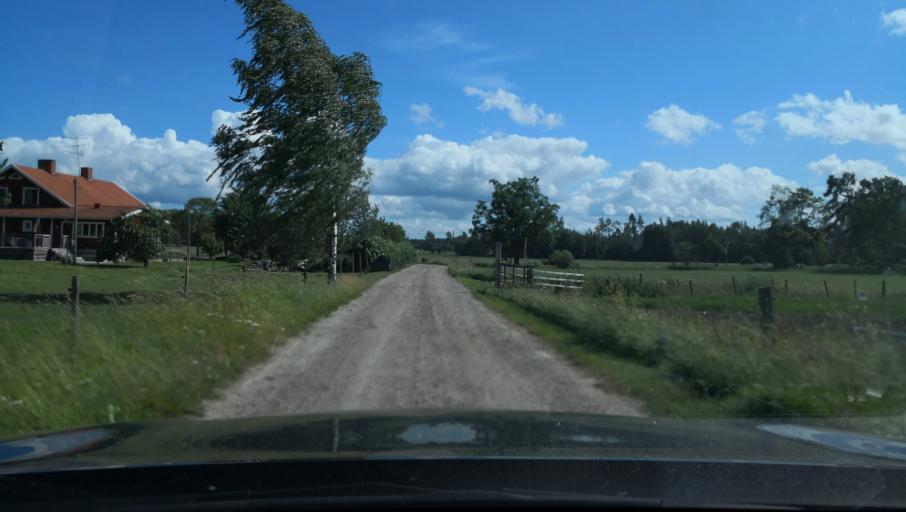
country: SE
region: Vaestmanland
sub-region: Kungsors Kommun
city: Kungsoer
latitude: 59.3221
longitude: 16.0579
